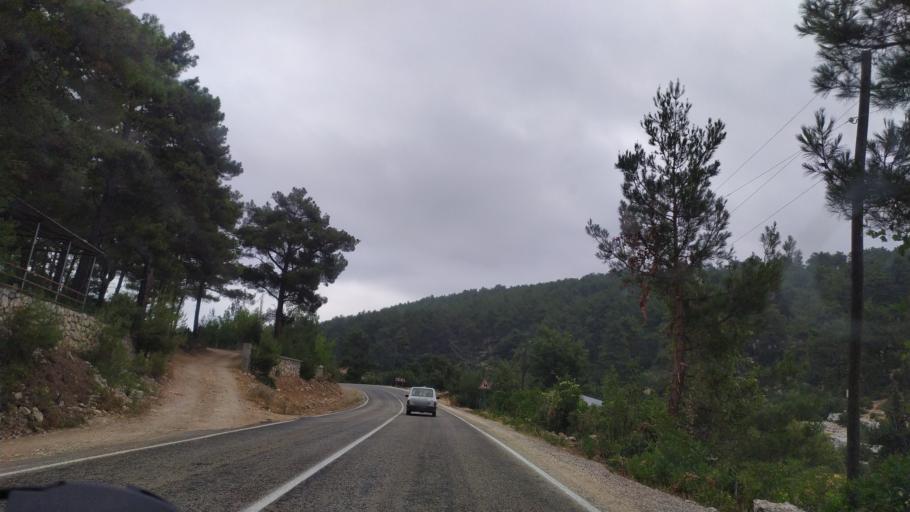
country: TR
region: Mersin
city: Silifke
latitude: 36.5394
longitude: 33.9408
